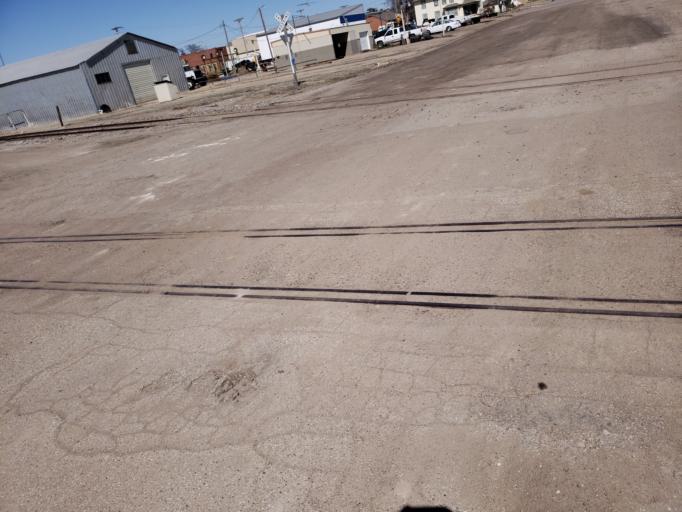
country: US
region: Kansas
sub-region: Ness County
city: Ness City
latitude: 38.4518
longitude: -99.9008
